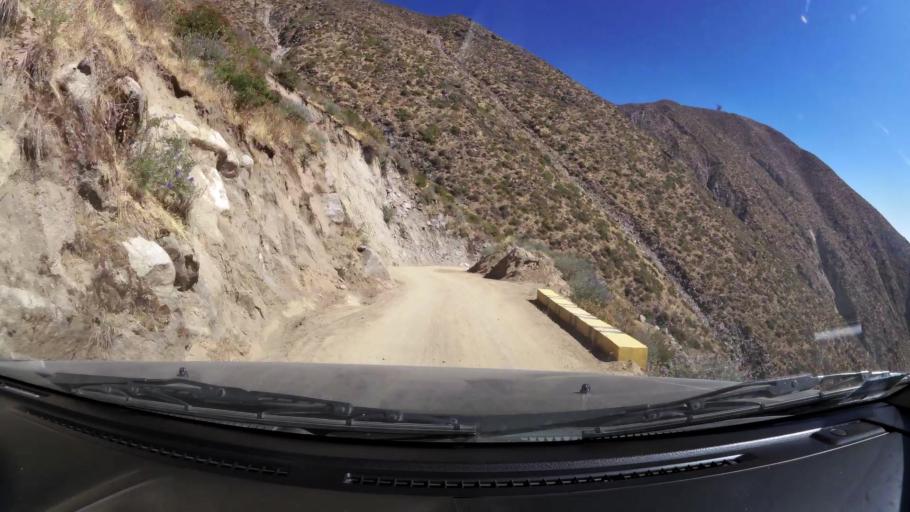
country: PE
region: Huancavelica
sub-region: Huaytara
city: Quito-Arma
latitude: -13.6196
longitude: -75.3535
